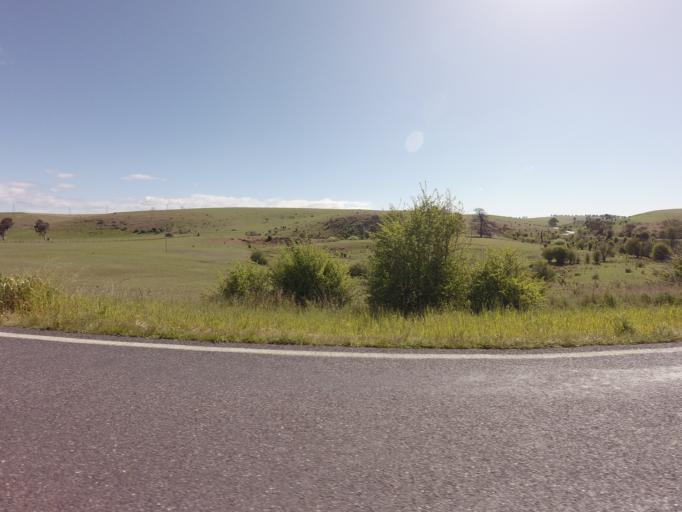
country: AU
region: Tasmania
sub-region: Derwent Valley
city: New Norfolk
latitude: -42.6539
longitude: 146.9358
